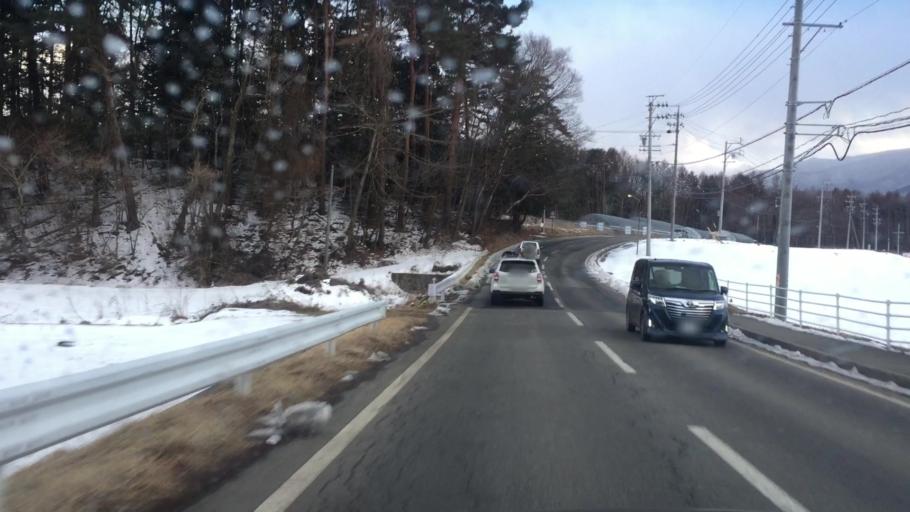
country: JP
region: Nagano
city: Chino
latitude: 35.9542
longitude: 138.2140
